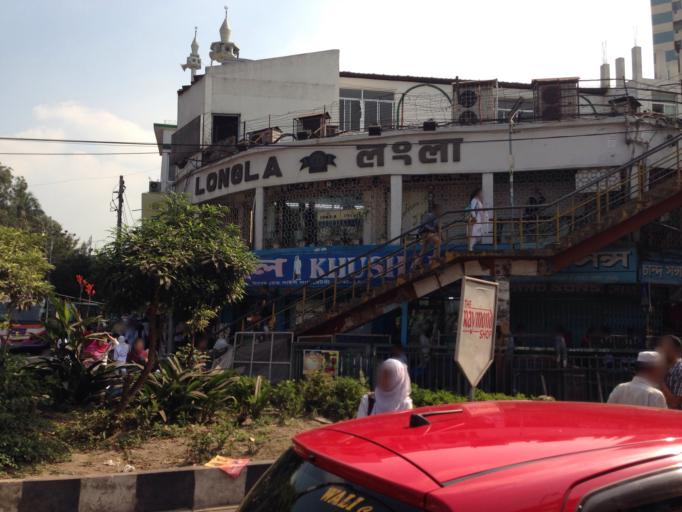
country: BD
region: Dhaka
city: Azimpur
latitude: 23.7388
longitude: 90.3836
